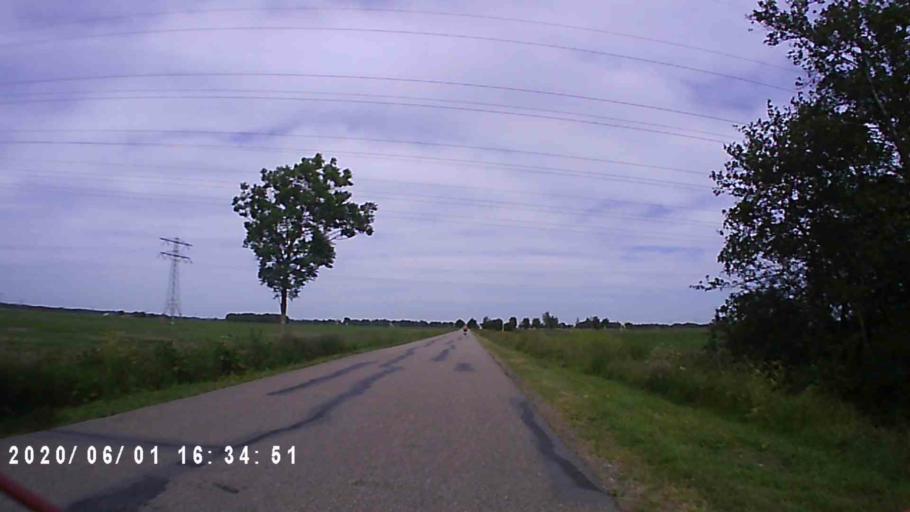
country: NL
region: Friesland
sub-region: Gemeente Leeuwarden
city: Camminghaburen
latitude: 53.1928
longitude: 5.8738
